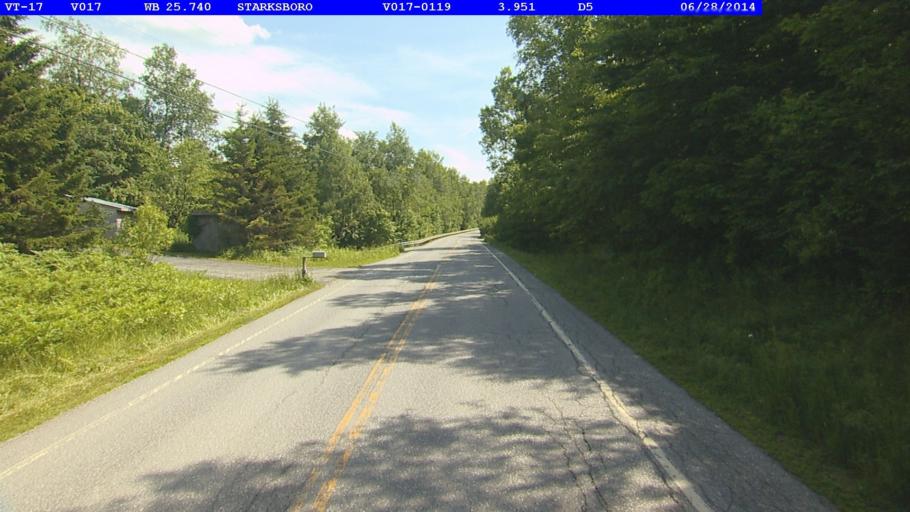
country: US
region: Vermont
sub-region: Addison County
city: Bristol
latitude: 44.1961
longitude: -72.9655
